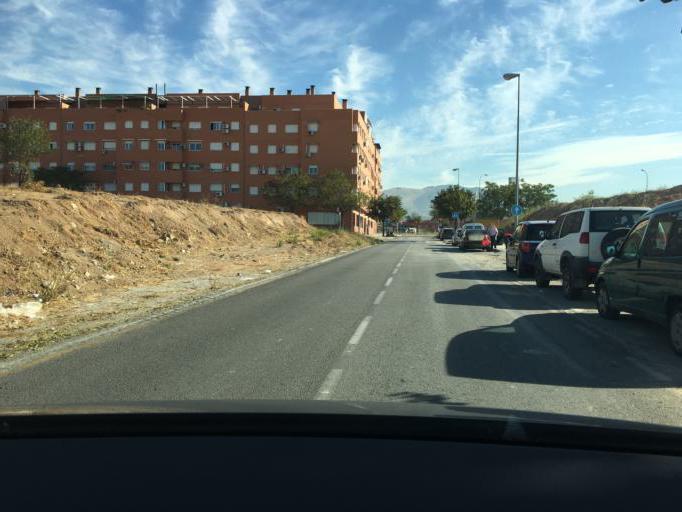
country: ES
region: Andalusia
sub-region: Provincia de Granada
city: Maracena
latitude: 37.2041
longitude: -3.6211
